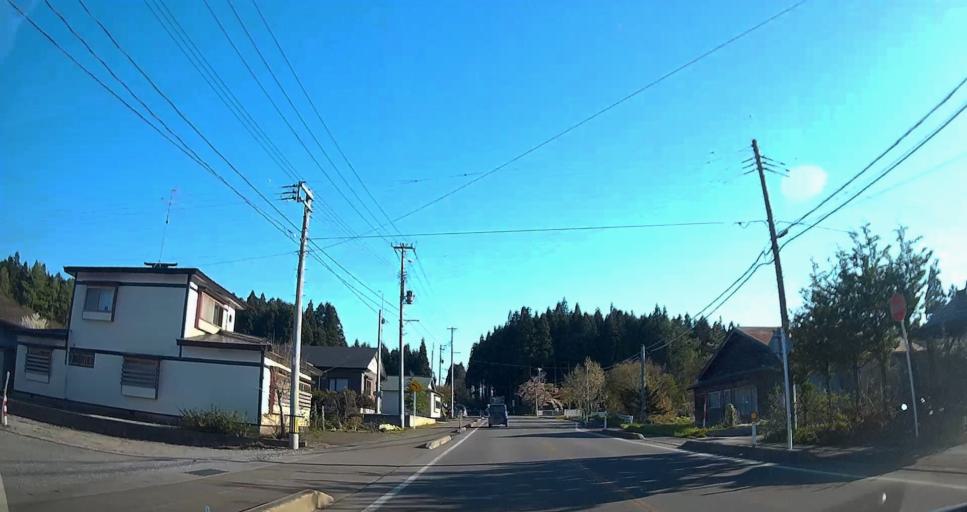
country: JP
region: Aomori
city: Mutsu
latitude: 41.3261
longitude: 141.2174
